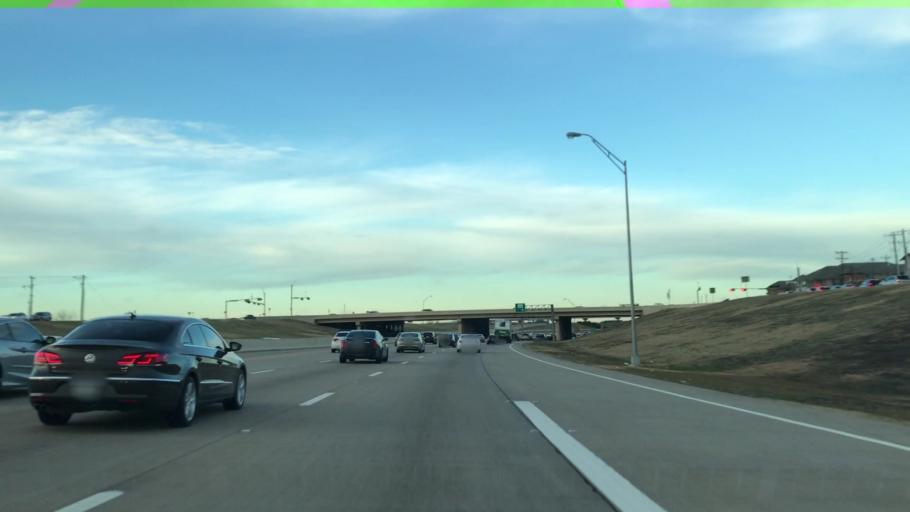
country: US
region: Texas
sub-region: Denton County
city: The Colony
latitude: 33.0449
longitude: -96.9223
